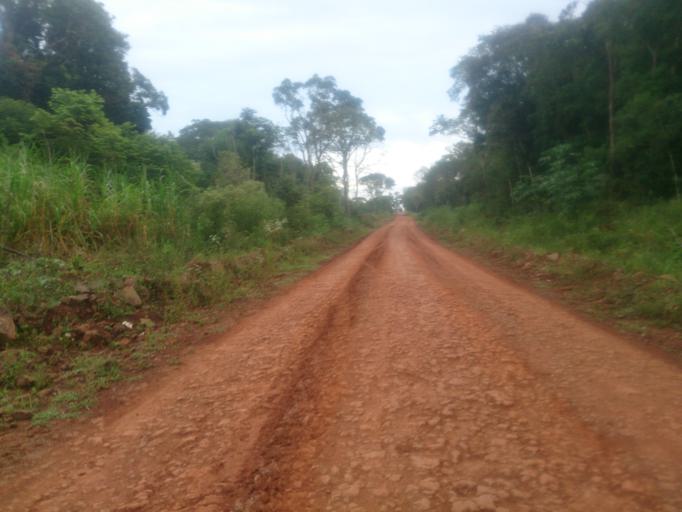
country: AR
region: Misiones
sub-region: Departamento de Obera
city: Obera
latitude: -27.4597
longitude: -55.1061
